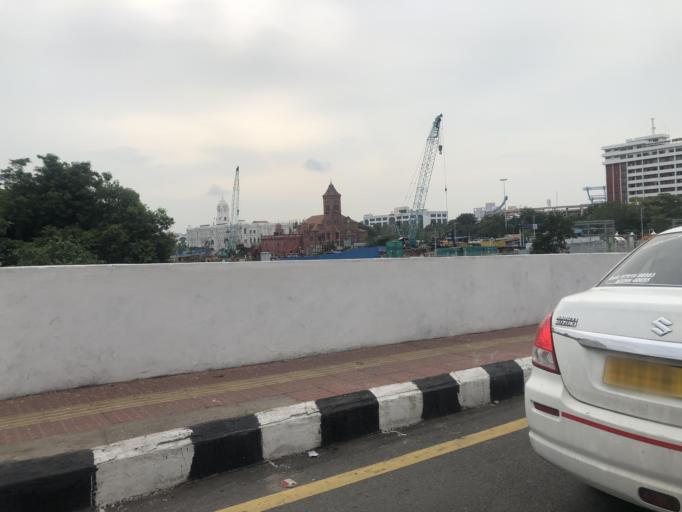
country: IN
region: Tamil Nadu
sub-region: Chennai
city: Chennai
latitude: 13.0805
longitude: 80.2752
